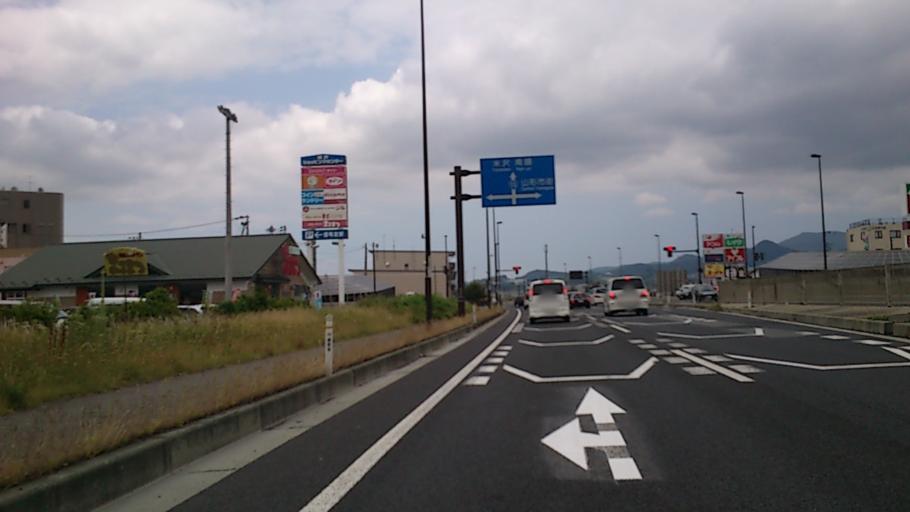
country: JP
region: Yamagata
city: Yamagata-shi
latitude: 38.2095
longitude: 140.3179
